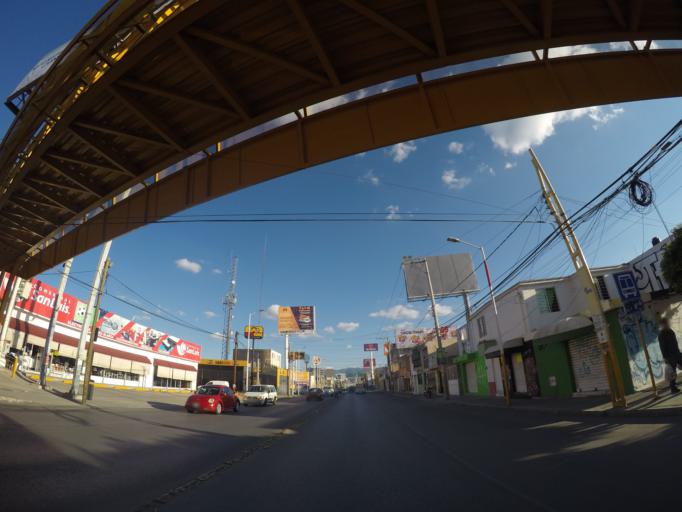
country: MX
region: San Luis Potosi
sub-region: San Luis Potosi
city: San Luis Potosi
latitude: 22.1680
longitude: -101.0017
